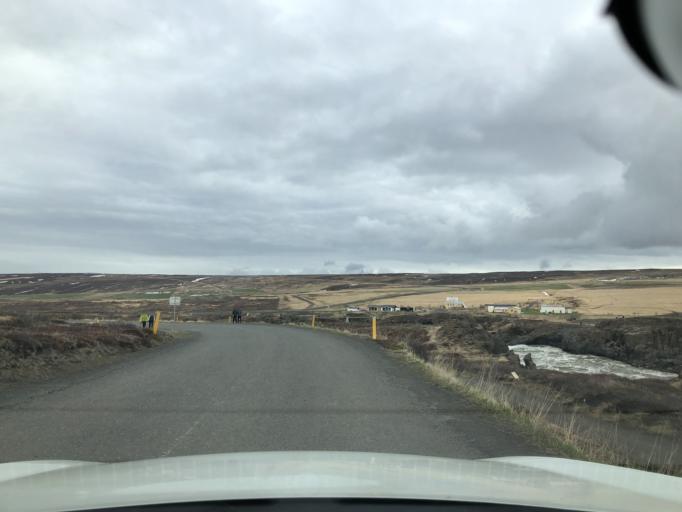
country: IS
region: Northeast
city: Laugar
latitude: 65.6844
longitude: -17.5484
